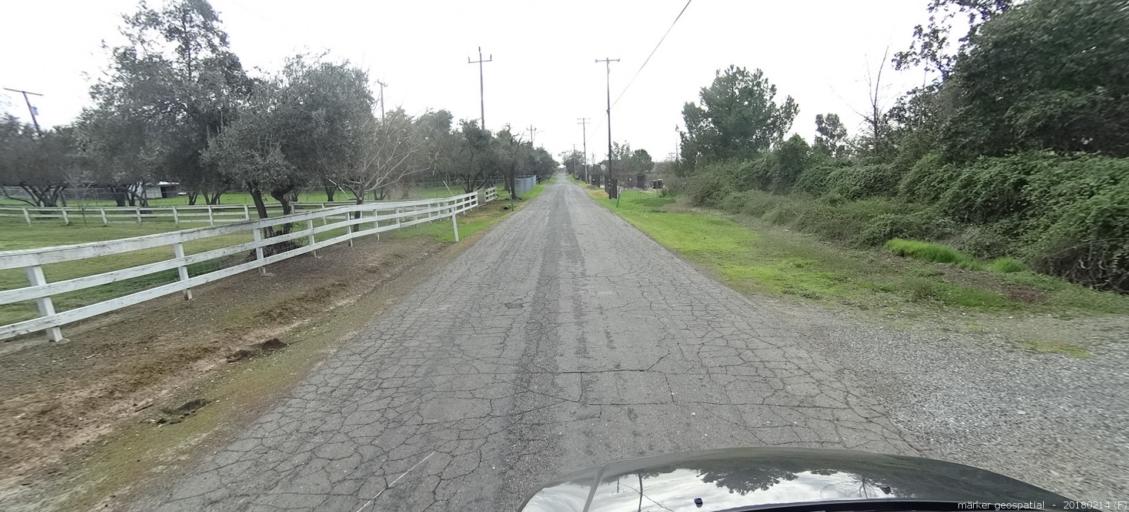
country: US
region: California
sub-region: Sacramento County
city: Rio Linda
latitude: 38.6737
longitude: -121.4754
